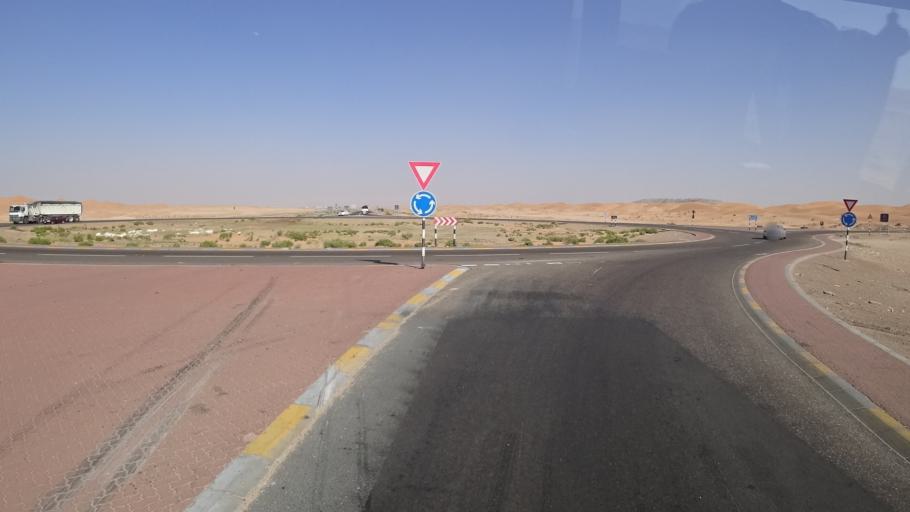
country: AE
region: Abu Dhabi
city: Al Ain
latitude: 24.0124
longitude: 55.4716
